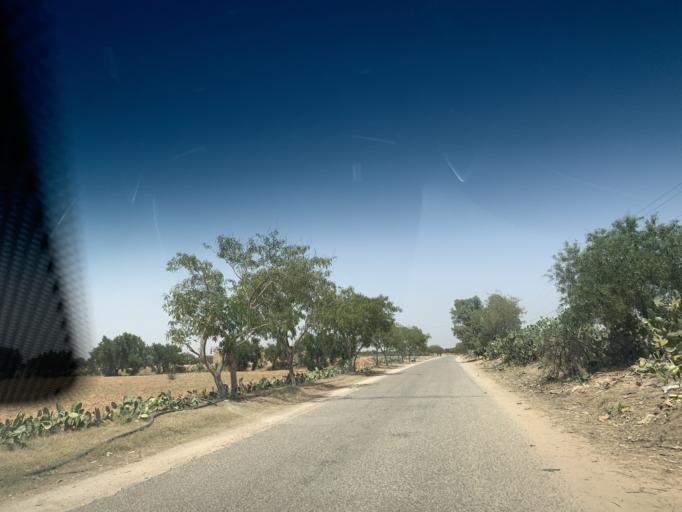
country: TN
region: Al Mahdiyah
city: Shurban
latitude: 35.1885
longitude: 10.2449
